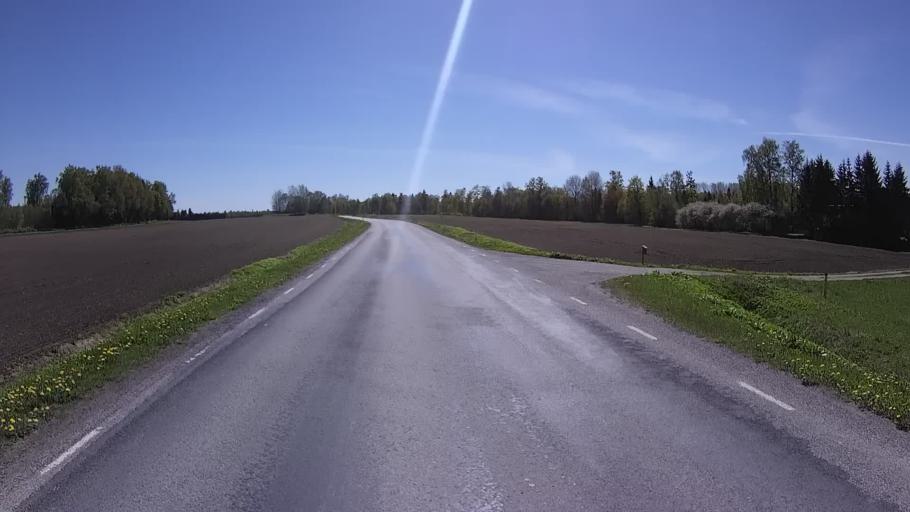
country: EE
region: Harju
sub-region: Raasiku vald
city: Raasiku
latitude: 59.0942
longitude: 25.1721
